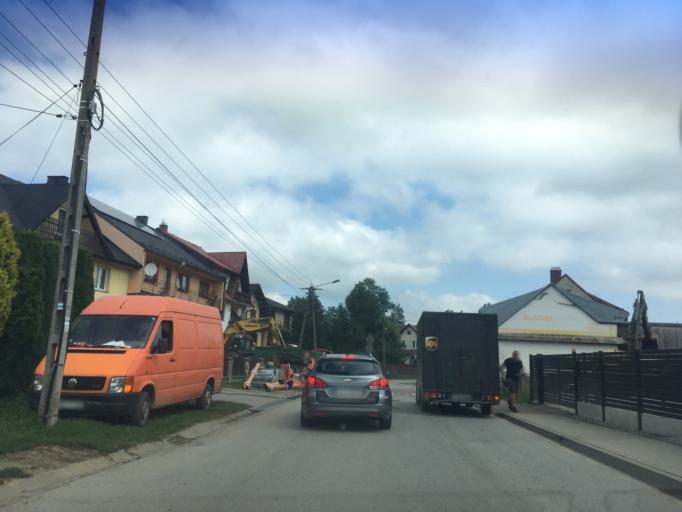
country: PL
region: Lesser Poland Voivodeship
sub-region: Powiat nowotarski
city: Lopuszna
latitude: 49.4370
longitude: 20.1377
